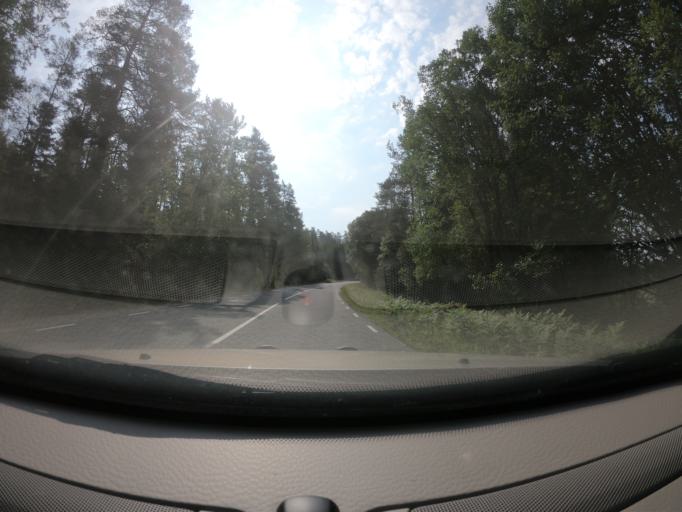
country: SE
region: Joenkoeping
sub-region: Vetlanda Kommun
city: Landsbro
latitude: 57.2632
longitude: 14.9347
